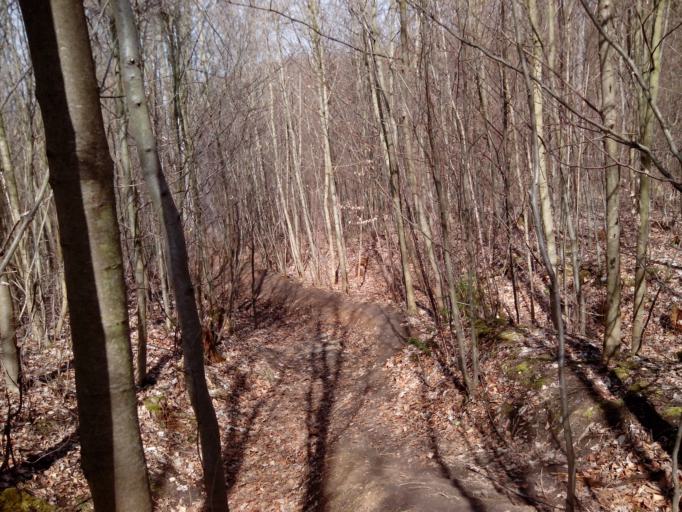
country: CZ
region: Central Bohemia
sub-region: Okres Beroun
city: Beroun
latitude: 49.9388
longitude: 14.1067
